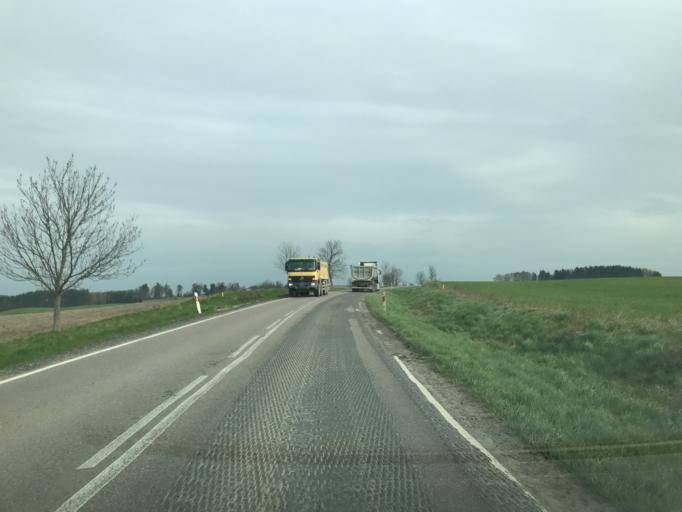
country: PL
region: Warmian-Masurian Voivodeship
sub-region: Powiat ostrodzki
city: Gierzwald
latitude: 53.5756
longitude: 20.0916
